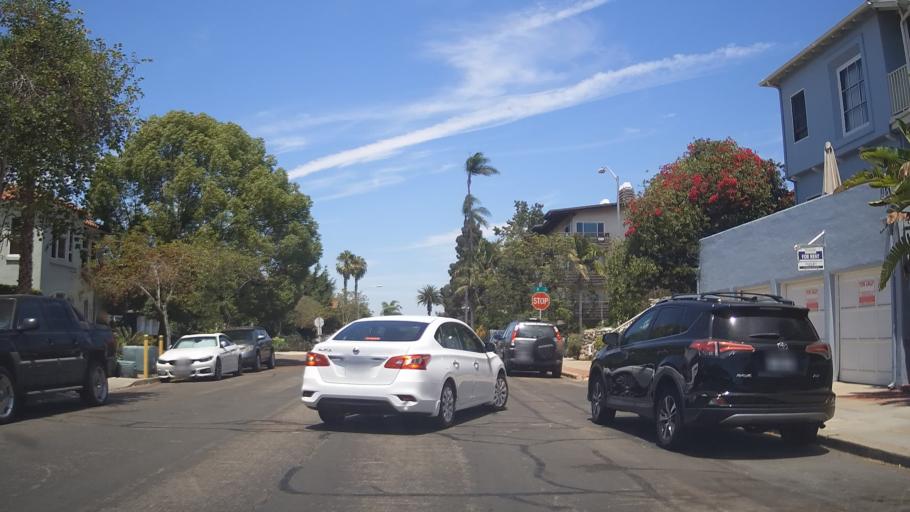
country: US
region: California
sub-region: San Diego County
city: San Diego
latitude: 32.7175
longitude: -117.1425
